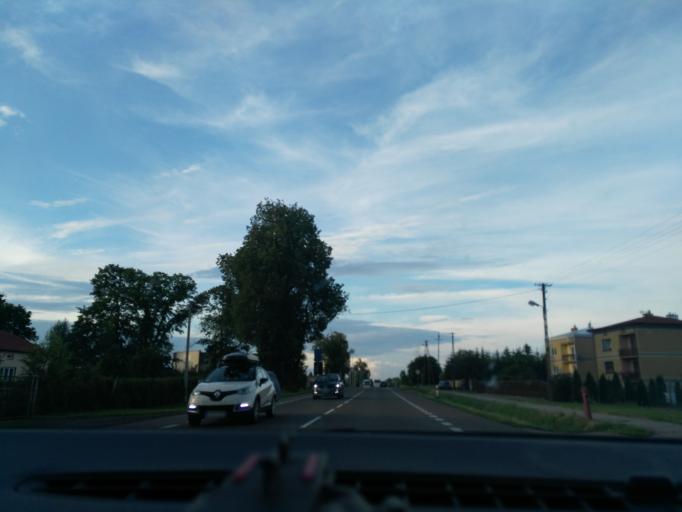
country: PL
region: Lublin Voivodeship
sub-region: Powiat lubelski
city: Niedrzwica Duza
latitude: 51.0931
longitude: 22.3661
